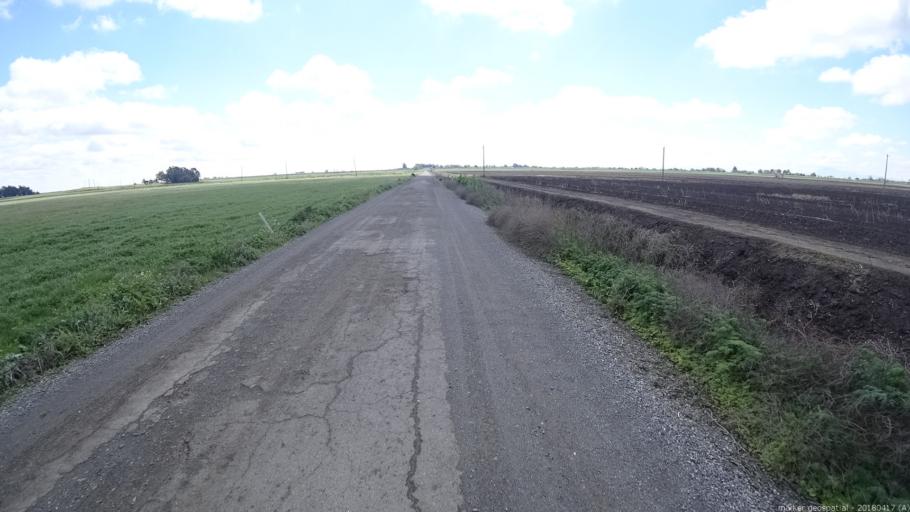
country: US
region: California
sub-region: Solano County
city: Rio Vista
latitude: 38.1450
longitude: -121.5829
